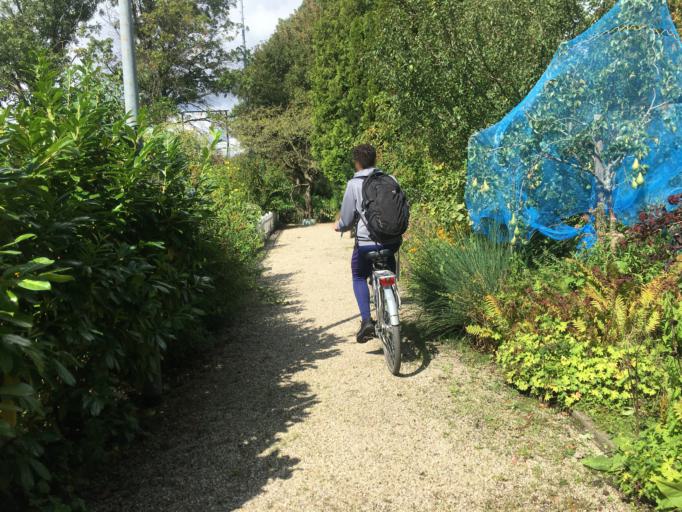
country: NL
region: North Holland
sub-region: Gemeente Diemen
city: Diemen
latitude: 52.3507
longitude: 4.9523
